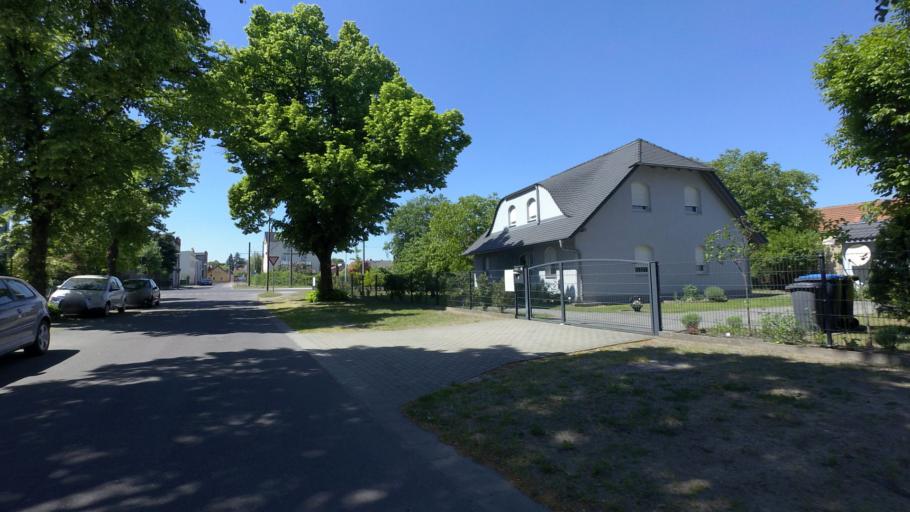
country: DE
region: Brandenburg
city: Cottbus
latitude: 51.7818
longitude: 14.3381
